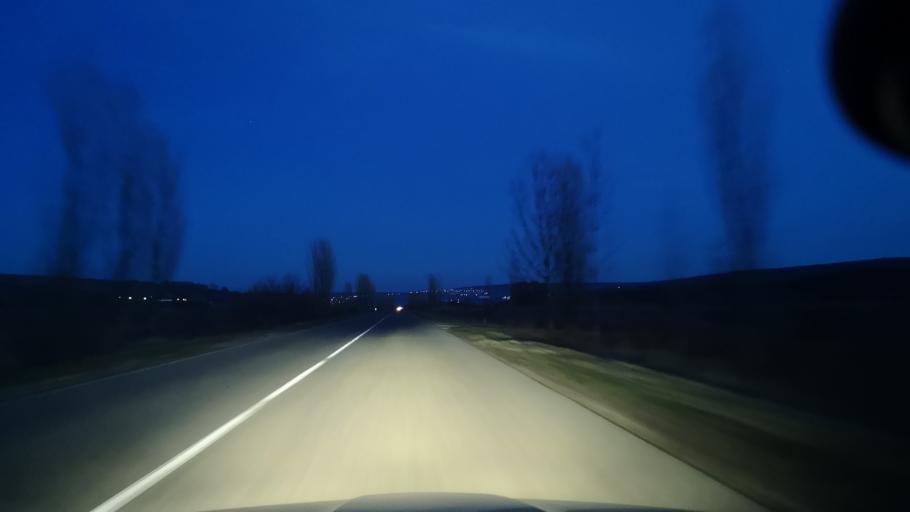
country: MD
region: Orhei
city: Orhei
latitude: 47.3442
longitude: 28.7335
